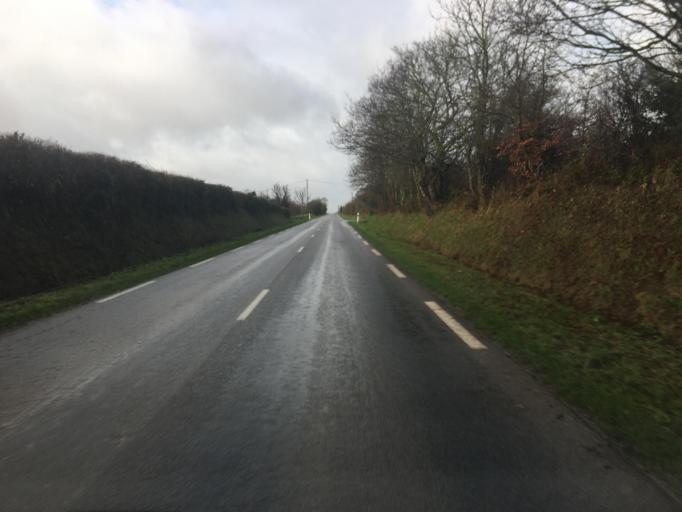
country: FR
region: Lower Normandy
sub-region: Departement de la Manche
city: Saint-Pierre-Eglise
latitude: 49.6689
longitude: -1.3681
